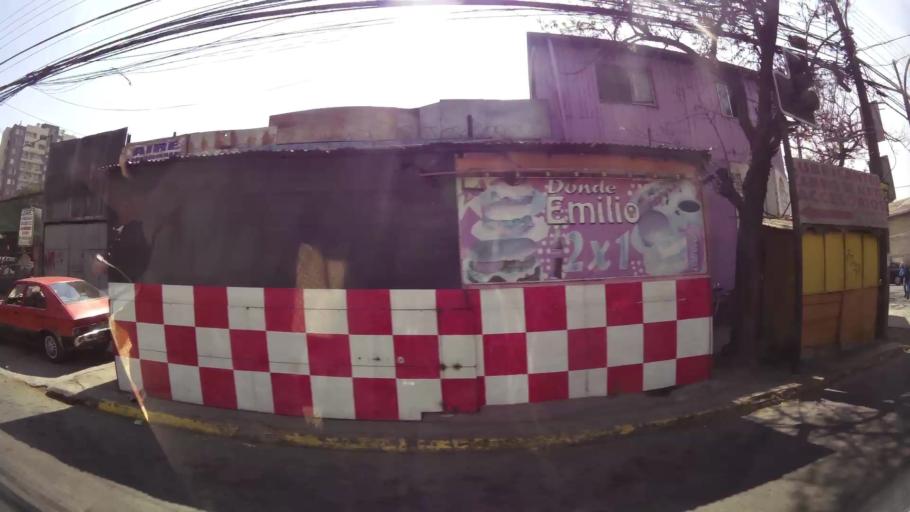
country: CL
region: Santiago Metropolitan
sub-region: Provincia de Santiago
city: Lo Prado
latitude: -33.4527
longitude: -70.6968
